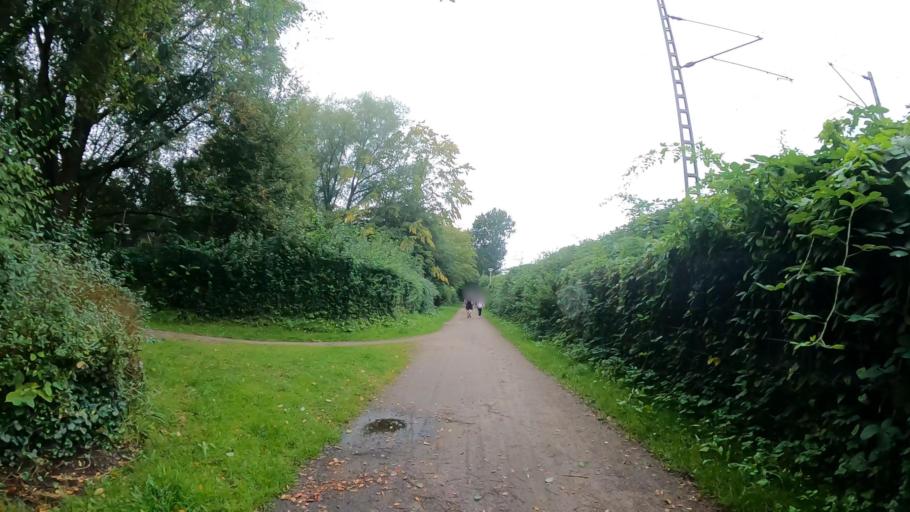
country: DE
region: Schleswig-Holstein
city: Rellingen
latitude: 53.6477
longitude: 9.8083
